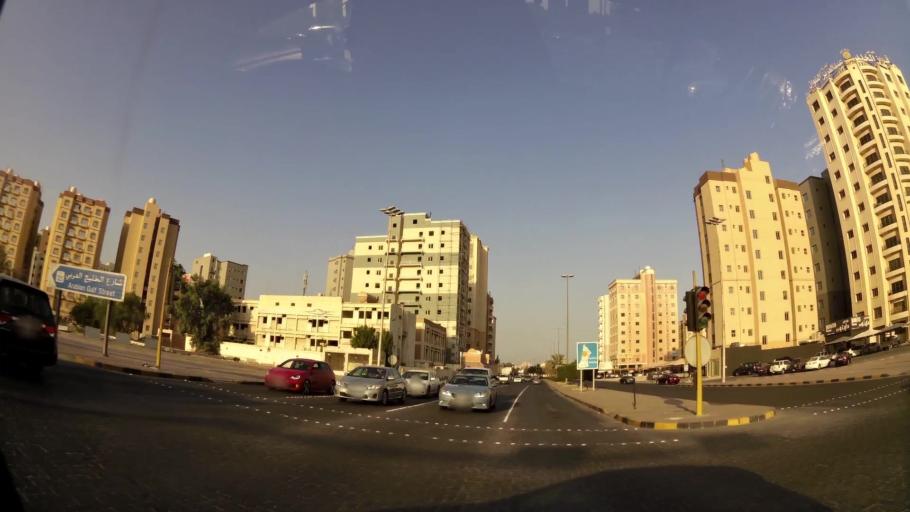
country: KW
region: Muhafazat Hawalli
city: As Salimiyah
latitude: 29.3355
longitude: 48.0717
